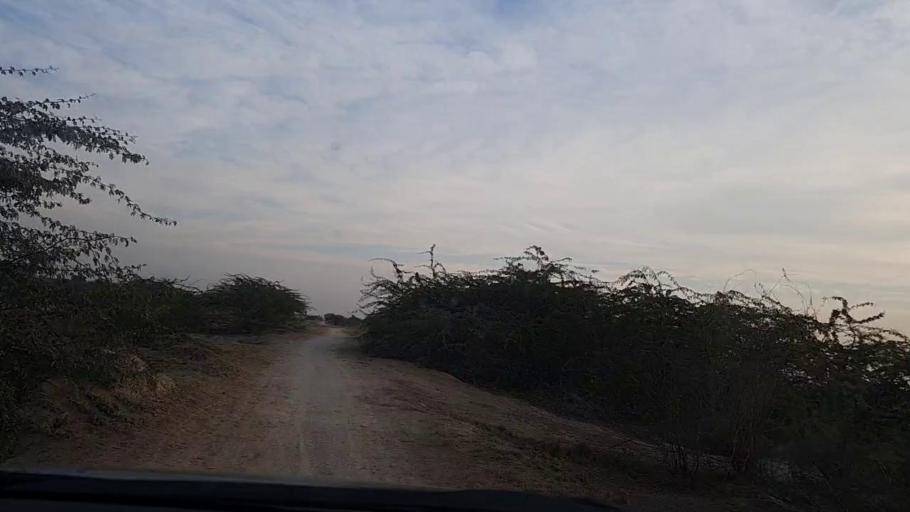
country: PK
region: Sindh
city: Sakrand
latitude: 26.1905
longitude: 68.3357
